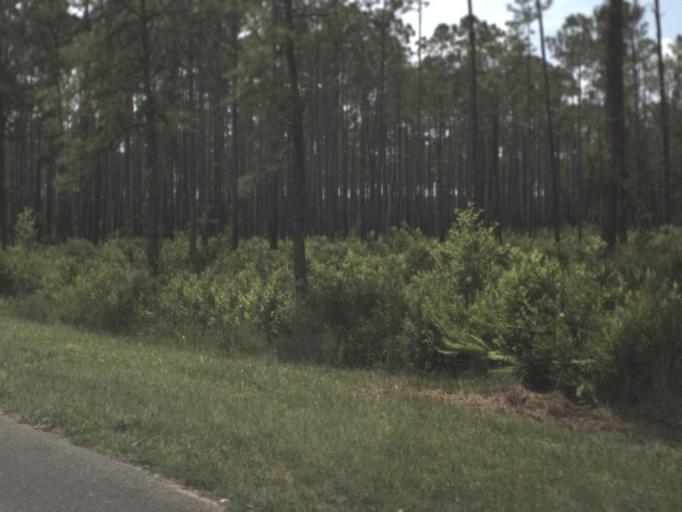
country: US
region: Florida
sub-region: Putnam County
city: Palatka
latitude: 29.4623
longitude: -81.7384
